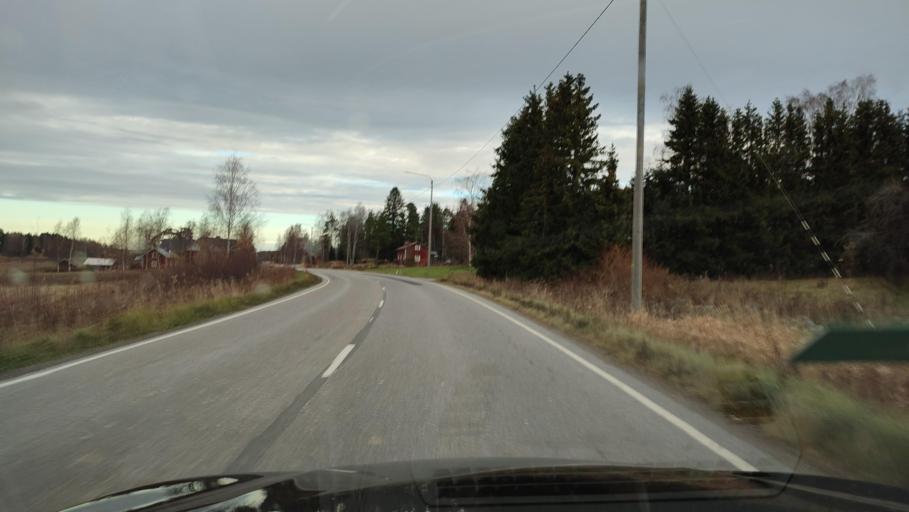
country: FI
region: Ostrobothnia
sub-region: Sydosterbotten
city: Naerpes
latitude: 62.4261
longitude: 21.3447
